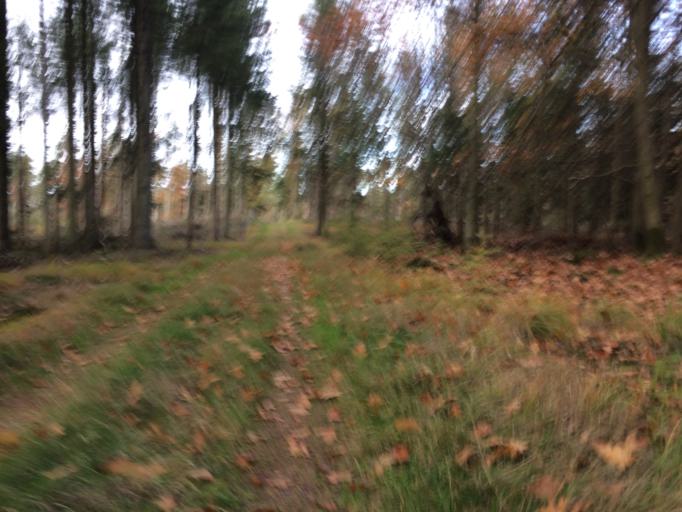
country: DK
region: Central Jutland
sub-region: Holstebro Kommune
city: Ulfborg
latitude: 56.2130
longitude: 8.4443
